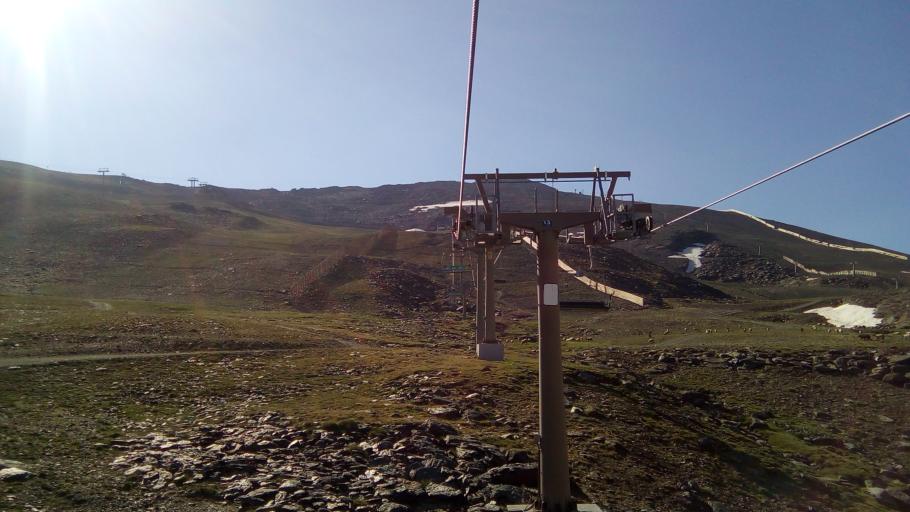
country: ES
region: Andalusia
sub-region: Provincia de Granada
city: Capileira
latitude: 37.0661
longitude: -3.3794
